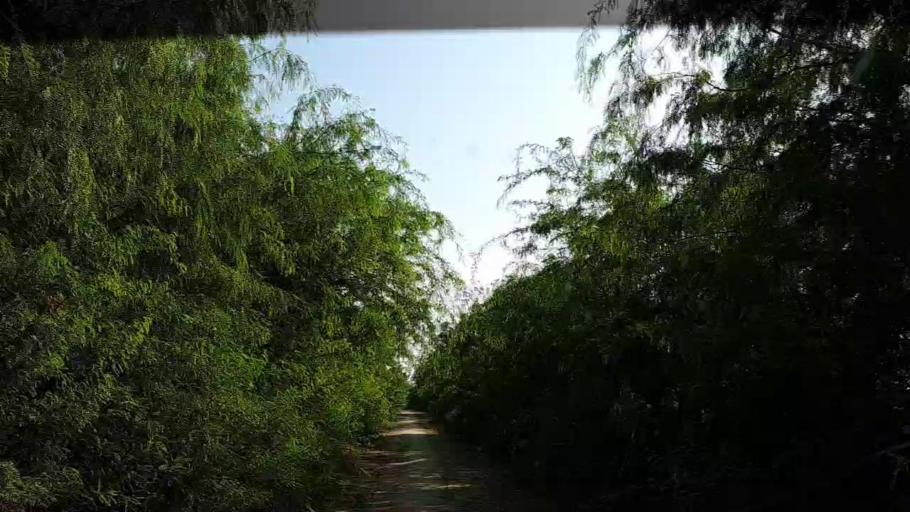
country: PK
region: Sindh
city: Adilpur
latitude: 27.9087
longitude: 69.2369
